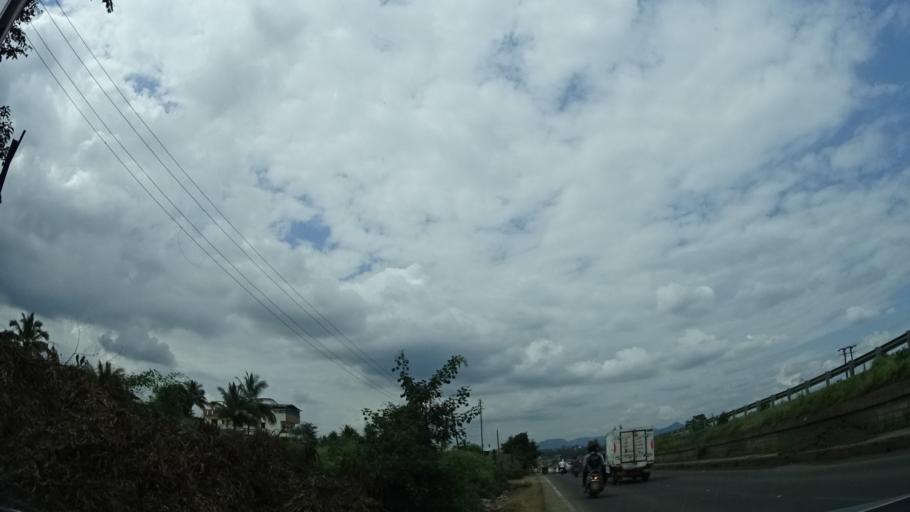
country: IN
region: Maharashtra
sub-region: Satara Division
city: Satara
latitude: 17.7024
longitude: 74.0257
